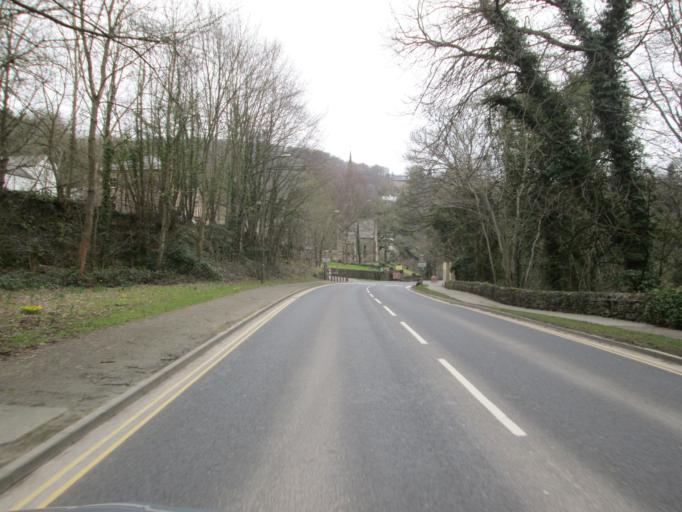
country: GB
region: England
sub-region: Derbyshire
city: Cromford
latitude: 53.1161
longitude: -1.5604
